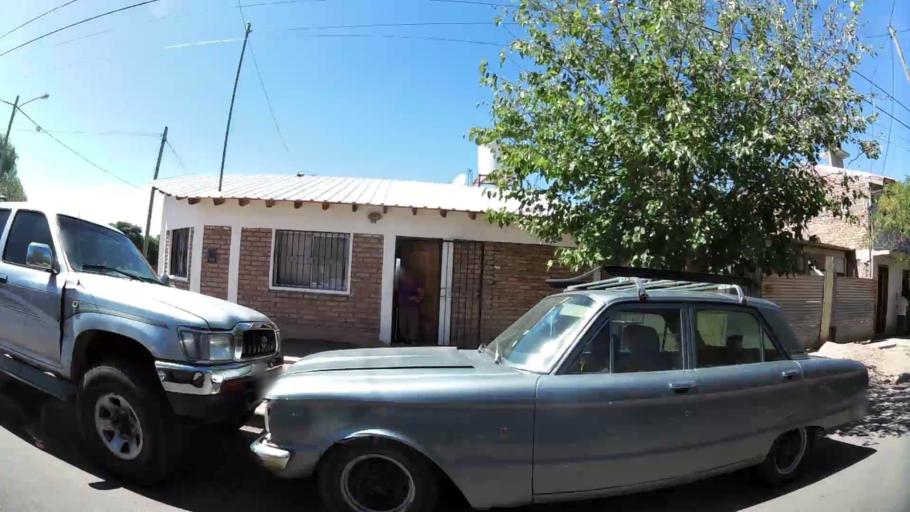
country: AR
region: Mendoza
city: Las Heras
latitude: -32.8498
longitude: -68.8713
